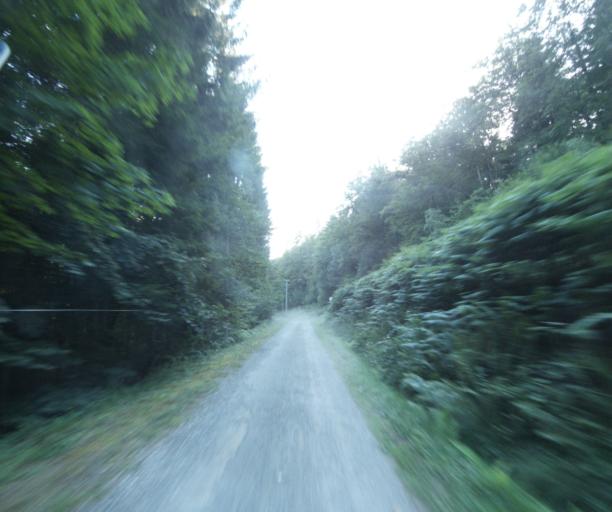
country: FR
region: Lorraine
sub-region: Departement des Vosges
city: Chantraine
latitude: 48.1429
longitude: 6.4299
